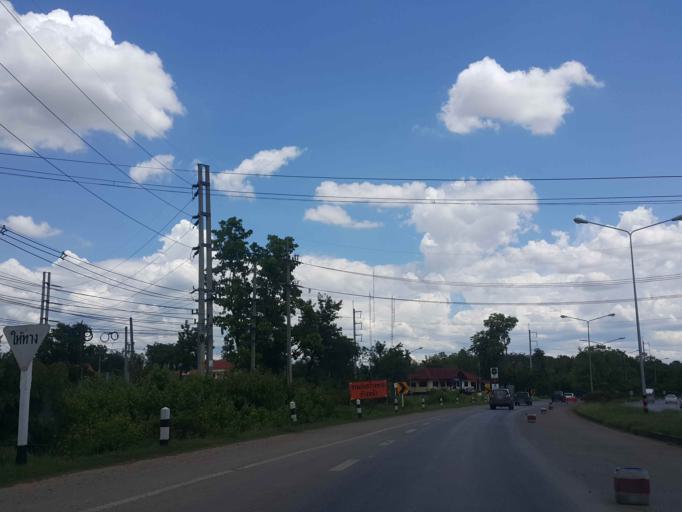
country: TH
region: Phrae
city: Nong Muang Khai
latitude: 18.2097
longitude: 100.1994
